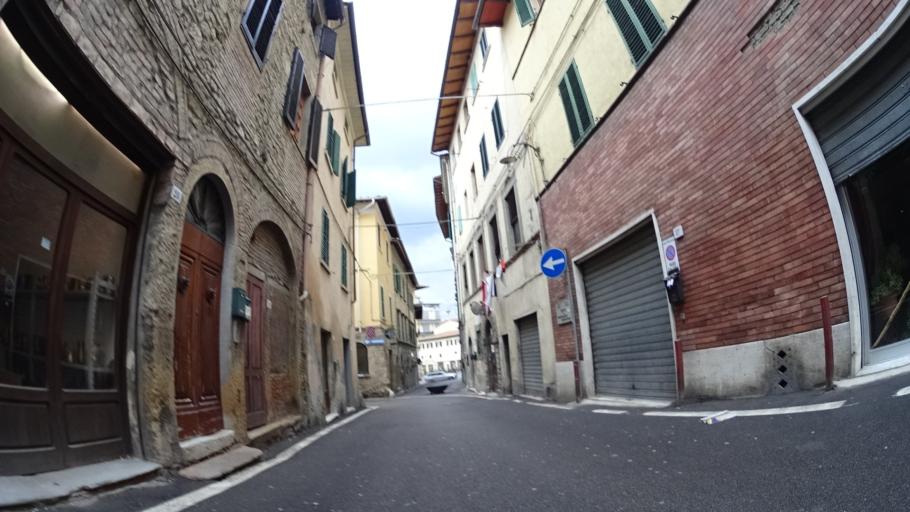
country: IT
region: Tuscany
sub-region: Provincia di Siena
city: Poggibonsi
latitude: 43.4675
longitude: 11.1457
